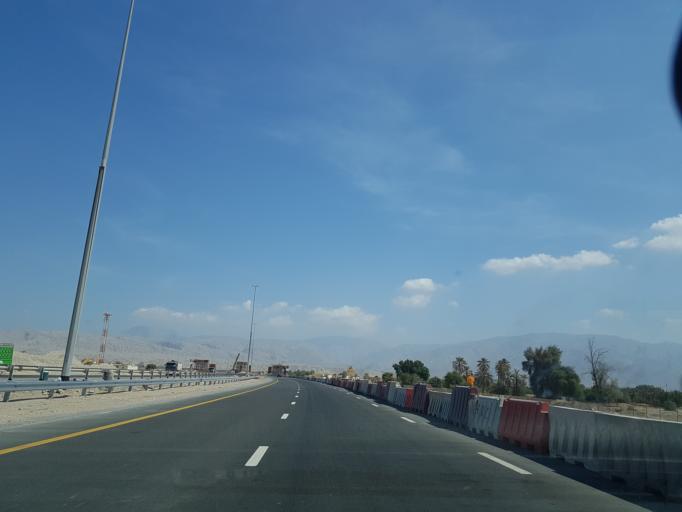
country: AE
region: Ra's al Khaymah
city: Ras al-Khaimah
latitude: 25.6975
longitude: 55.9838
